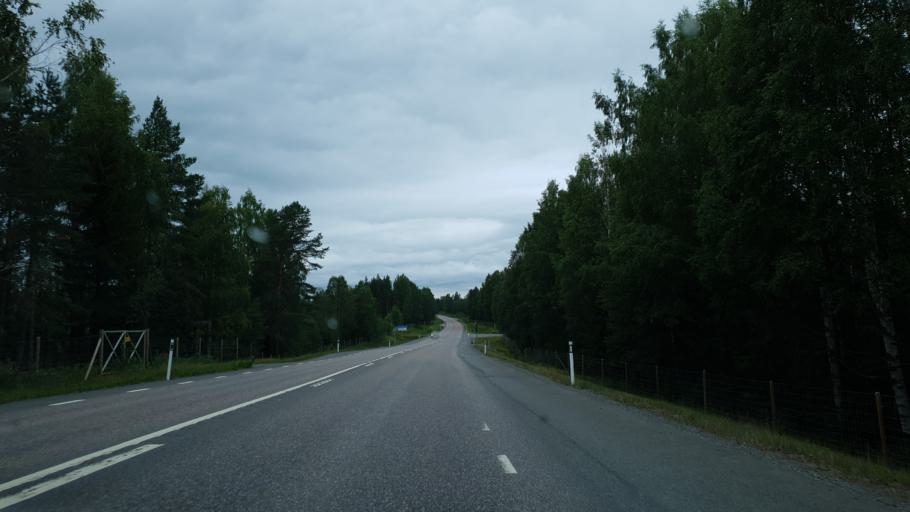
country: SE
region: Vaesterbotten
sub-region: Skelleftea Kommun
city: Viken
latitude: 64.7957
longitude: 20.7445
